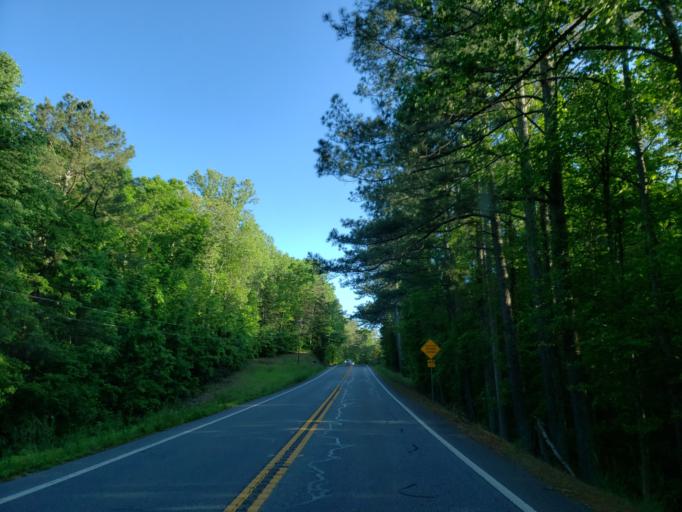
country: US
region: Georgia
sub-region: Cherokee County
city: Canton
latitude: 34.2679
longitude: -84.5853
